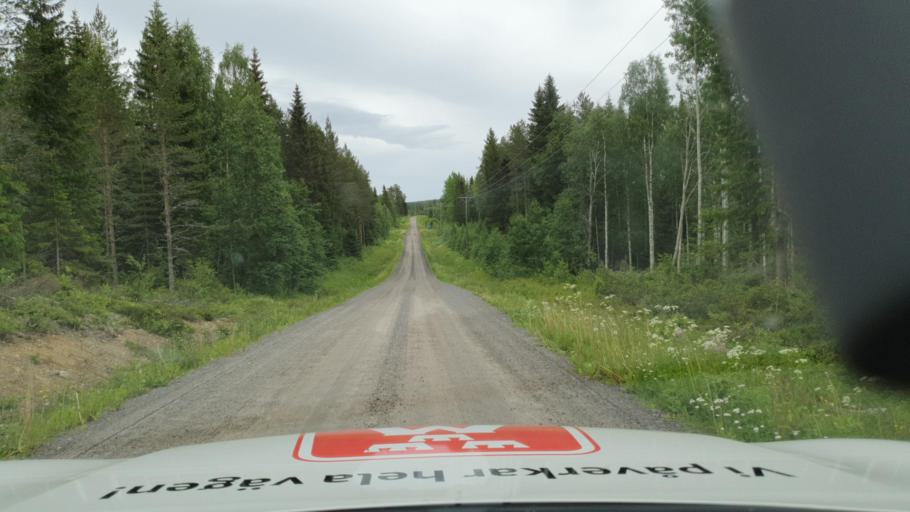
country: SE
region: Vaesterbotten
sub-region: Skelleftea Kommun
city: Burtraesk
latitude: 64.3454
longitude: 20.6048
